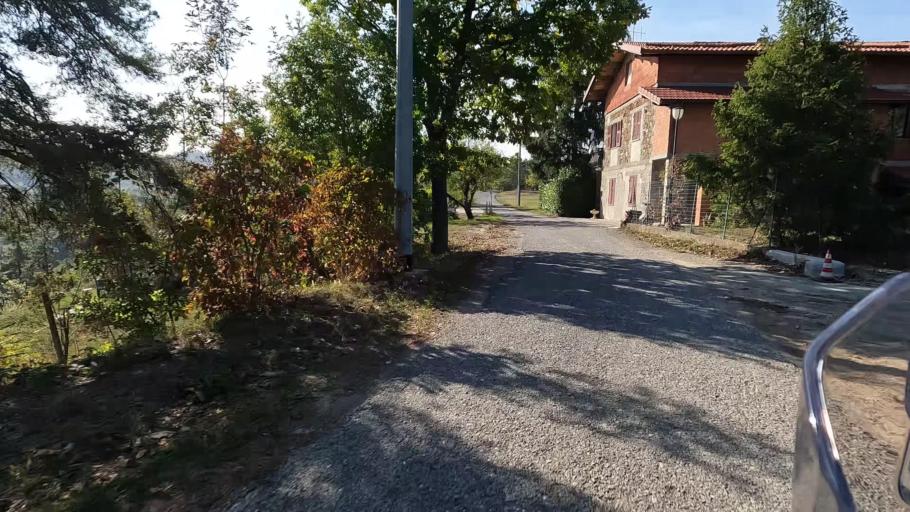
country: IT
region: Liguria
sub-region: Provincia di Savona
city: Urbe
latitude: 44.5276
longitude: 8.5409
